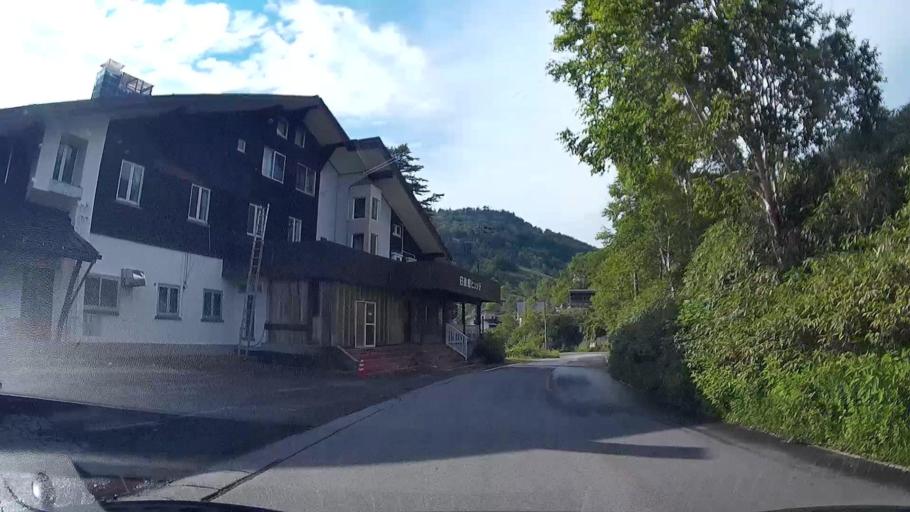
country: JP
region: Nagano
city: Nakano
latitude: 36.6382
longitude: 138.5108
